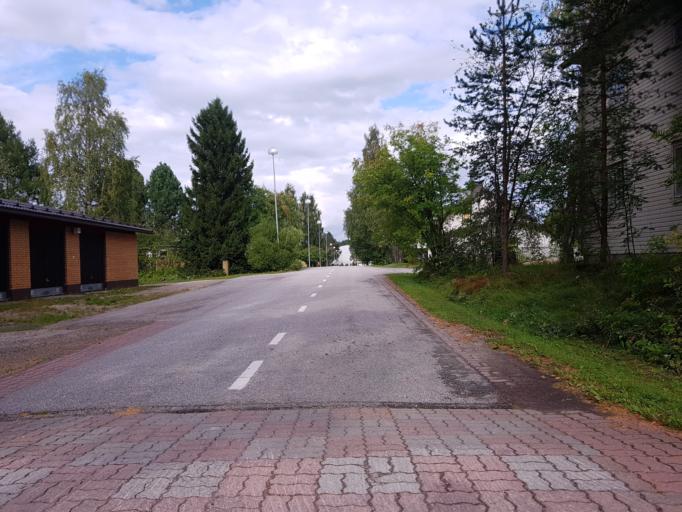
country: FI
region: Kainuu
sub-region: Kehys-Kainuu
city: Kuhmo
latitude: 64.1268
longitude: 29.5133
